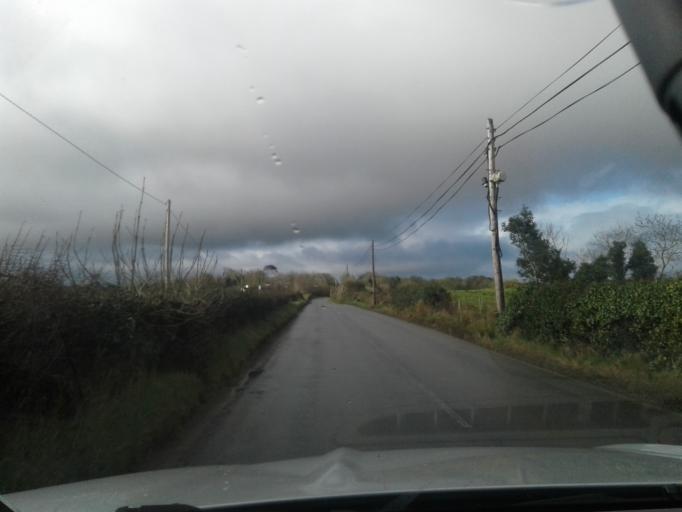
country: IE
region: Ulster
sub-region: County Donegal
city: Ramelton
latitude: 55.0518
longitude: -7.6393
